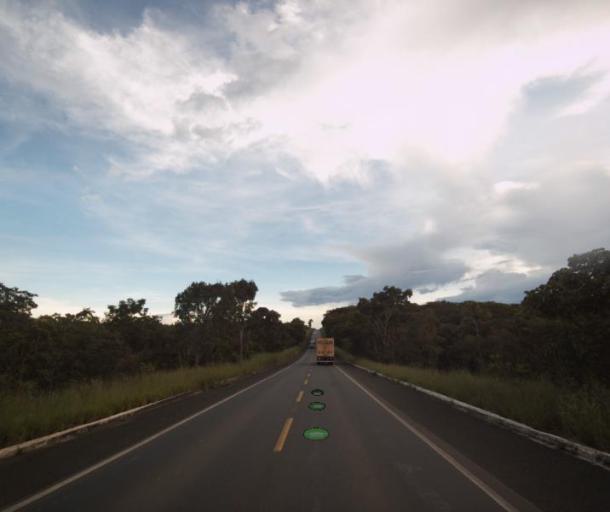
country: BR
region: Goias
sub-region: Uruacu
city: Uruacu
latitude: -14.1494
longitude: -49.1185
